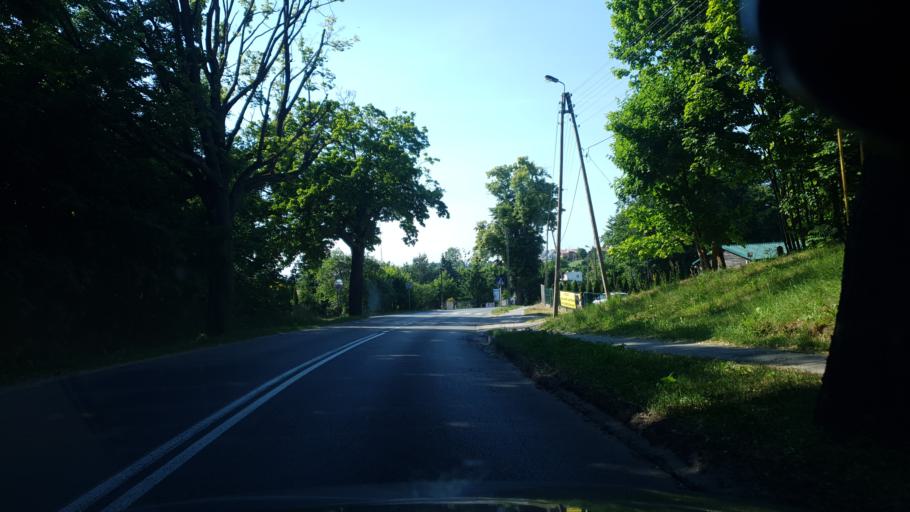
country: PL
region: Pomeranian Voivodeship
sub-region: Gdynia
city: Wielki Kack
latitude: 54.4360
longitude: 18.4640
